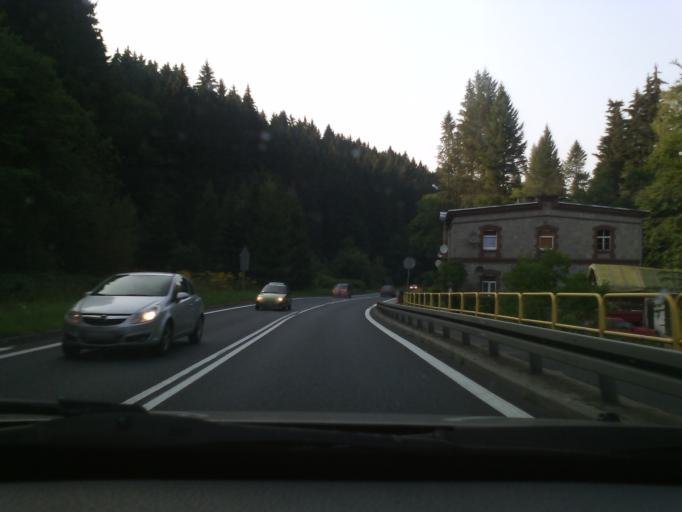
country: PL
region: Lower Silesian Voivodeship
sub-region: Powiat jeleniogorski
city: Piechowice
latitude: 50.8386
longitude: 15.5678
